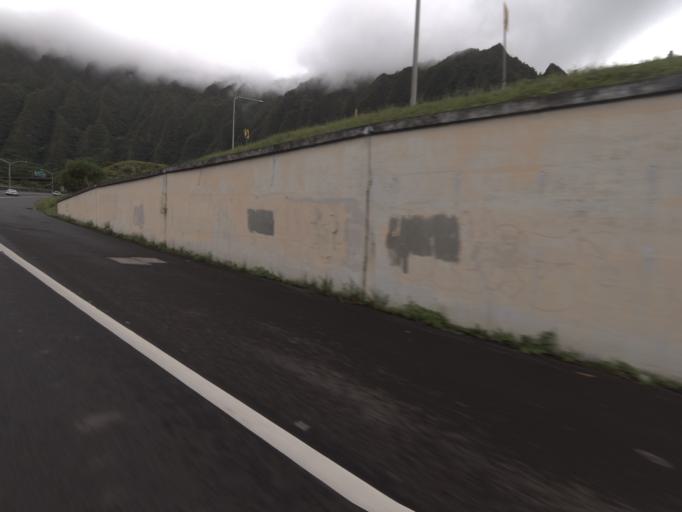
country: US
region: Hawaii
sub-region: Honolulu County
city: Kane'ohe
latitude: 21.3949
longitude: -157.8113
